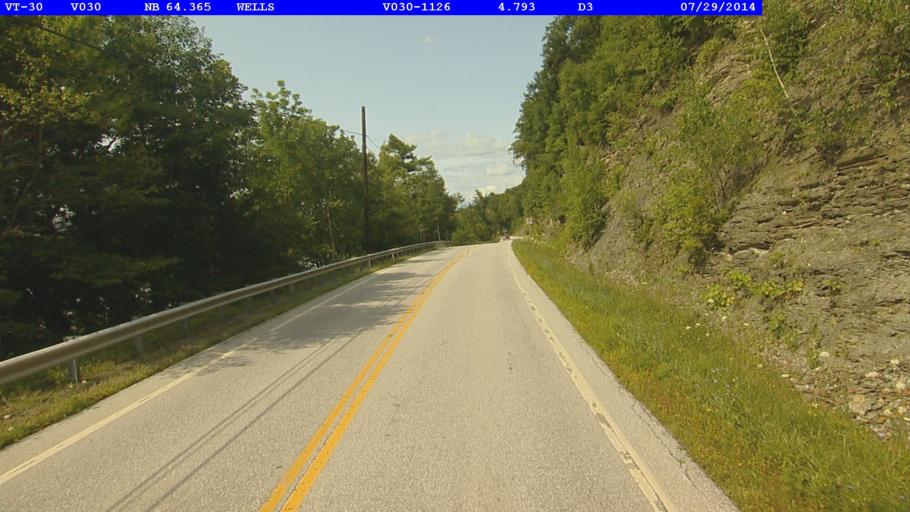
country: US
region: Vermont
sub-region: Rutland County
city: Poultney
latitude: 43.4598
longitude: -73.2057
